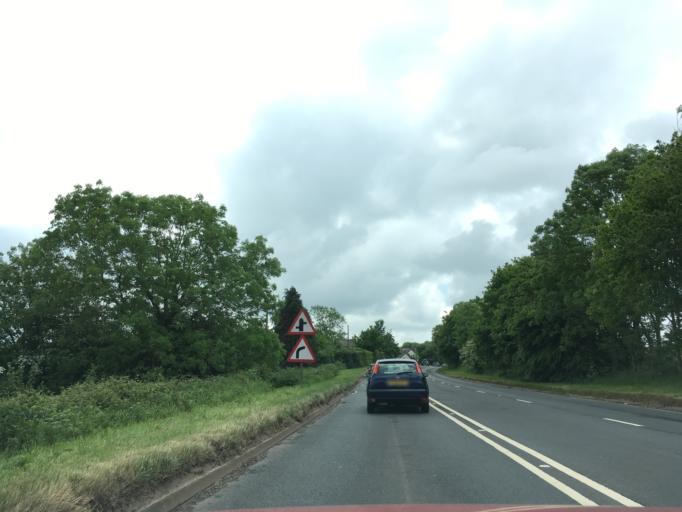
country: GB
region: England
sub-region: Devon
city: Uffculme
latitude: 50.9247
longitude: -3.3247
